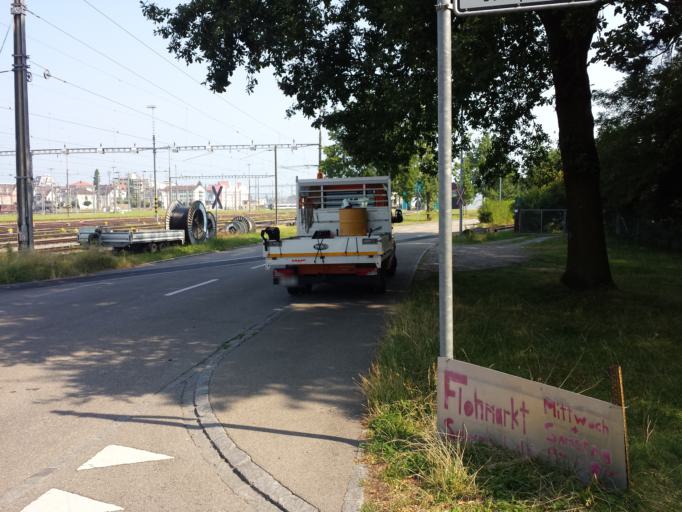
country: CH
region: Thurgau
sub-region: Arbon District
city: Romanshorn
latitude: 47.5578
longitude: 9.3788
